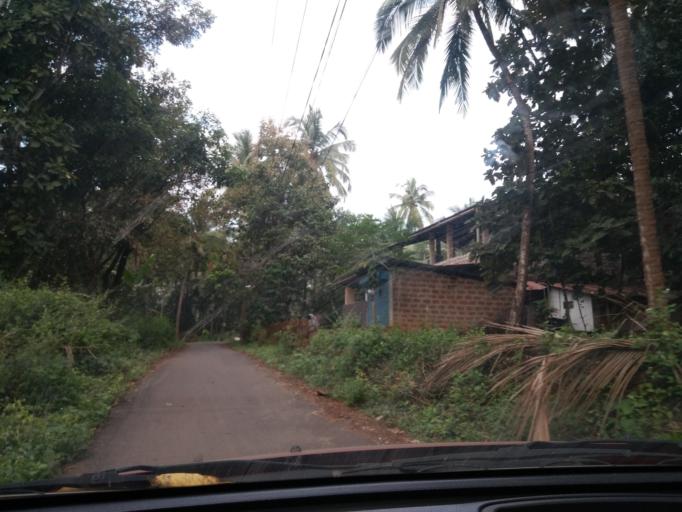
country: IN
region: Goa
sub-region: South Goa
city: Varca
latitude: 15.2287
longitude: 73.9515
